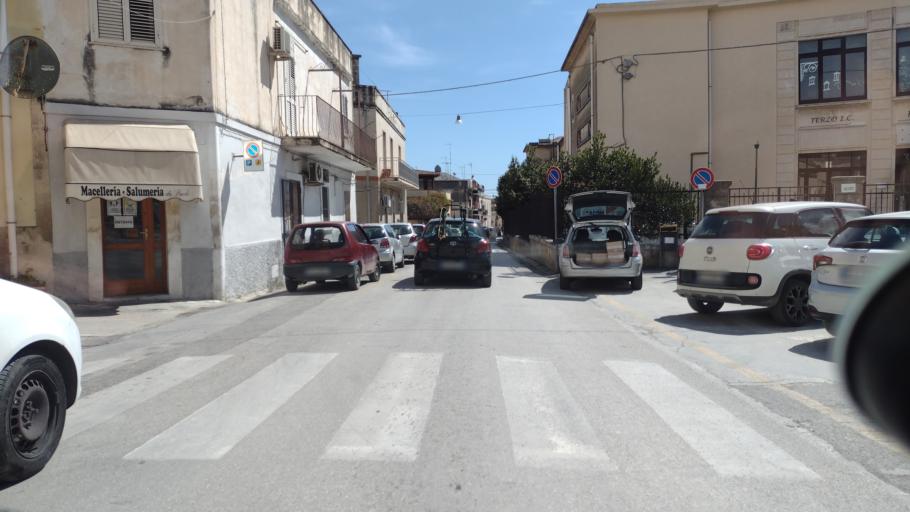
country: IT
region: Sicily
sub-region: Provincia di Siracusa
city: Noto
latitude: 36.8885
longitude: 15.0702
